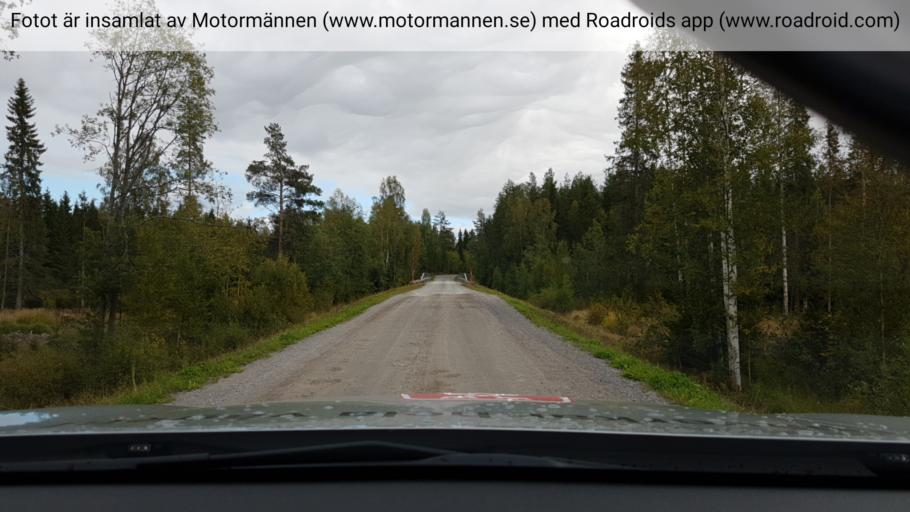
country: SE
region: Vaesterbotten
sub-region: Skelleftea Kommun
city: Byske
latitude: 65.1055
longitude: 21.1765
